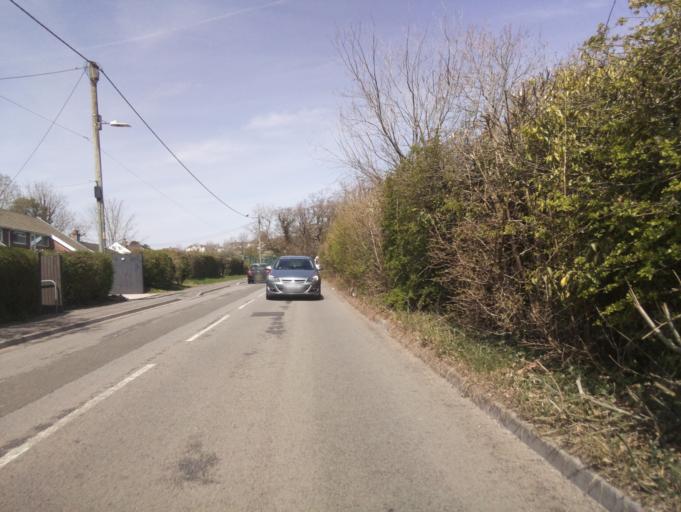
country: GB
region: Wales
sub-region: Merthyr Tydfil County Borough
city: Merthyr Tydfil
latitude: 51.7591
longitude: -3.3731
